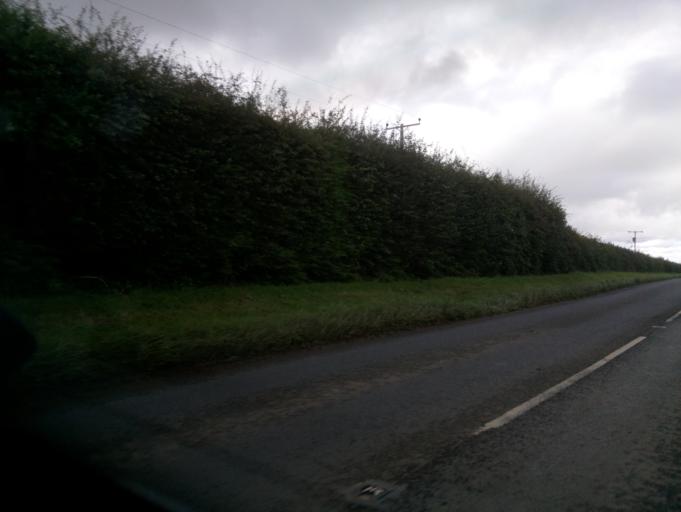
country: GB
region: England
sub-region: Devon
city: Kingsbridge
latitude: 50.3005
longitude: -3.7905
